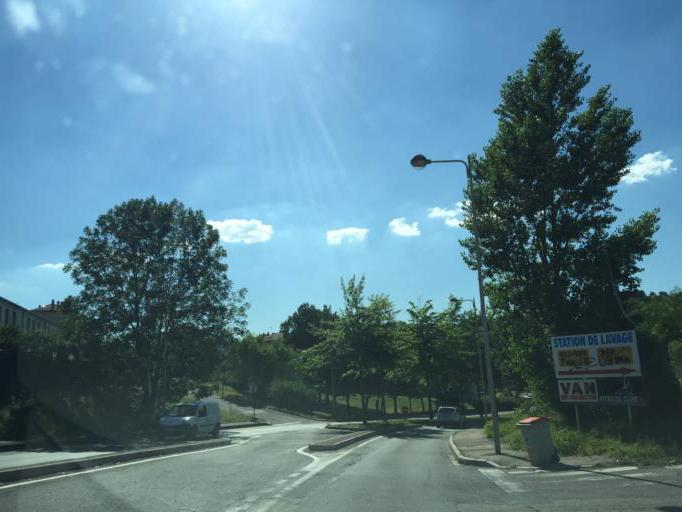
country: FR
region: Rhone-Alpes
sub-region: Departement de la Loire
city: Saint-Chamond
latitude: 45.4819
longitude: 4.5329
